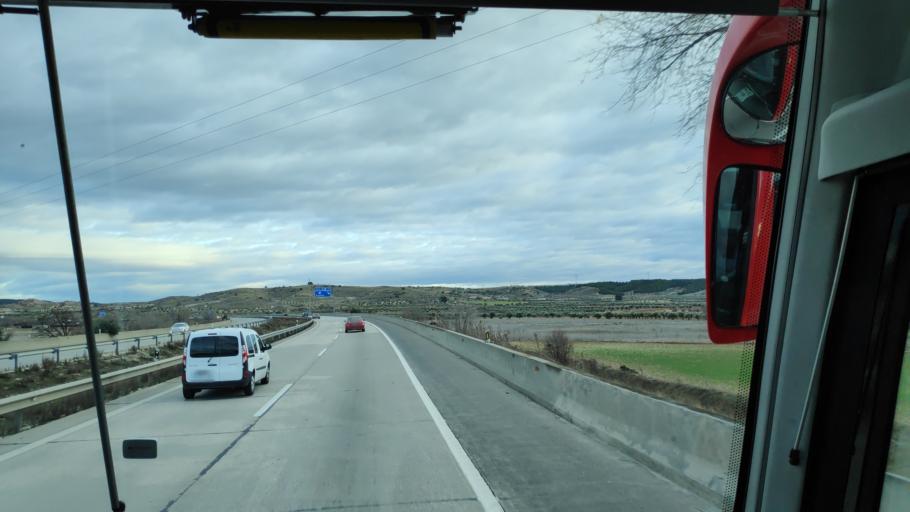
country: ES
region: Madrid
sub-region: Provincia de Madrid
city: Vaciamadrid
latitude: 40.3014
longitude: -3.4847
